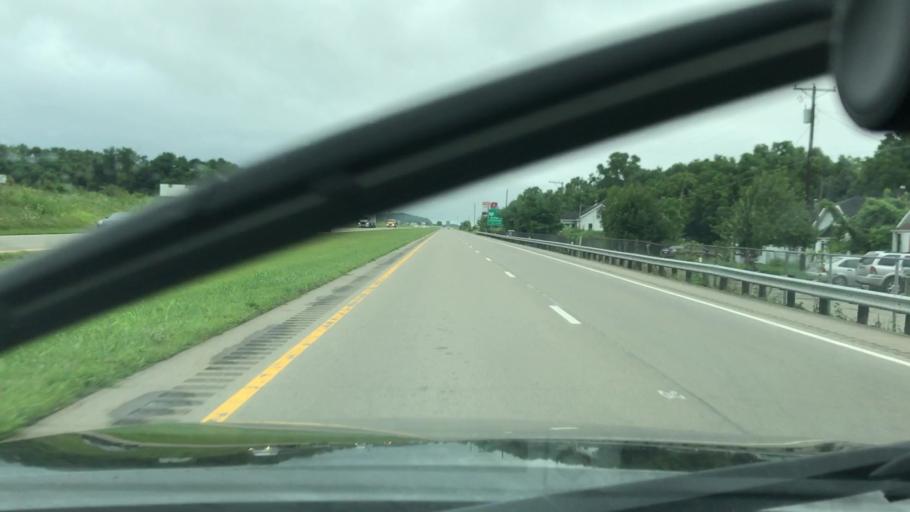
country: US
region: Ohio
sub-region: Ross County
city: Chillicothe
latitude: 39.4066
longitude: -82.9750
